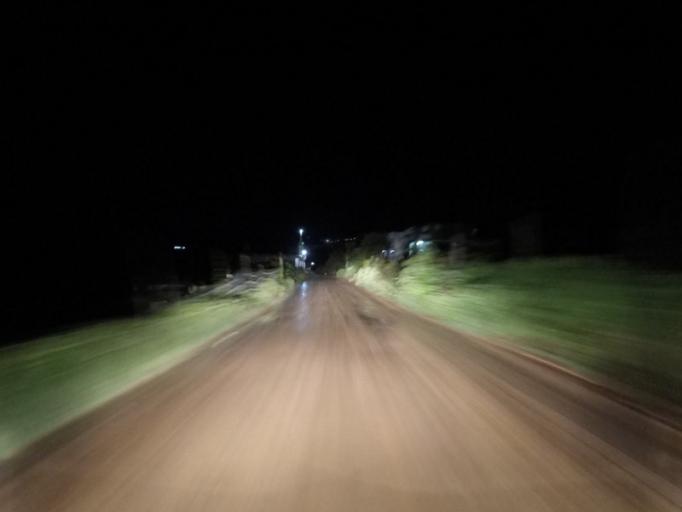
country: IN
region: Tamil Nadu
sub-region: Nilgiri
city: Kotagiri
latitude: 11.4823
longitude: 76.8226
